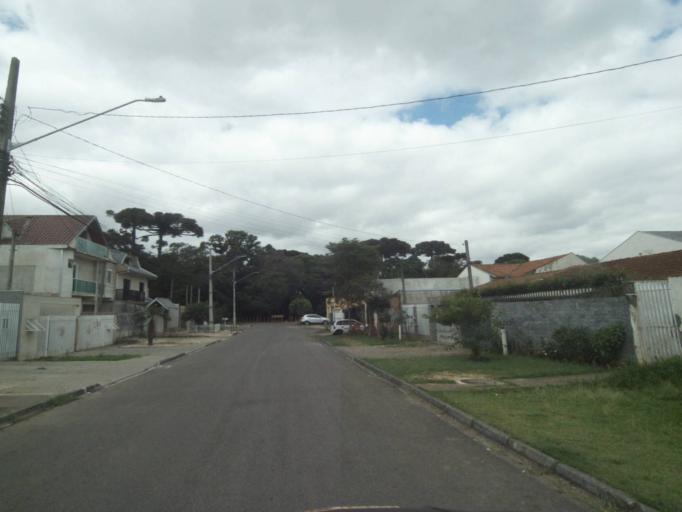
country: BR
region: Parana
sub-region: Sao Jose Dos Pinhais
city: Sao Jose dos Pinhais
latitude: -25.5577
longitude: -49.2594
